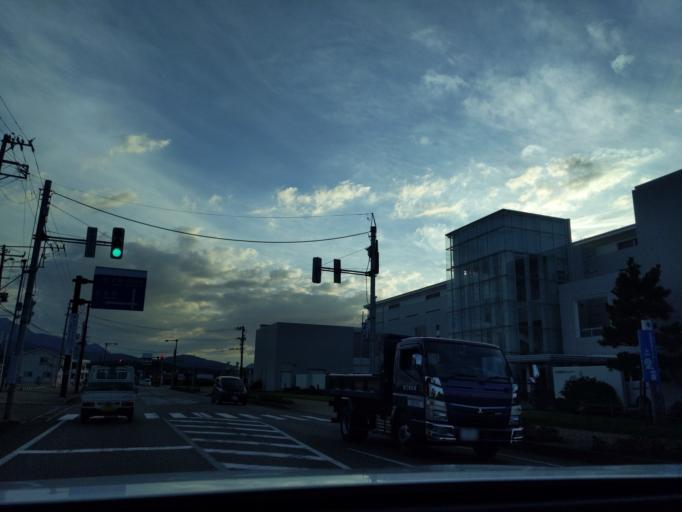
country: JP
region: Niigata
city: Kashiwazaki
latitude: 37.3716
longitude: 138.5479
